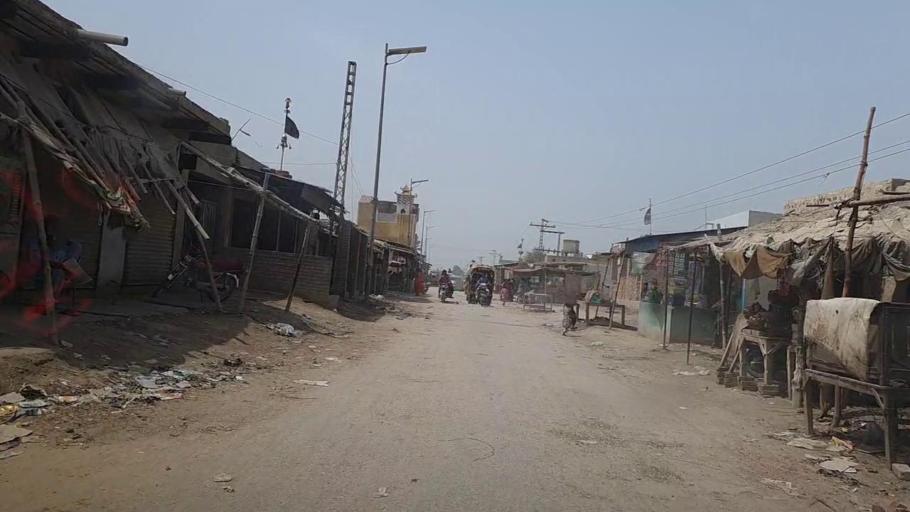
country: PK
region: Sindh
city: Radhan
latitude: 27.1713
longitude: 67.9469
